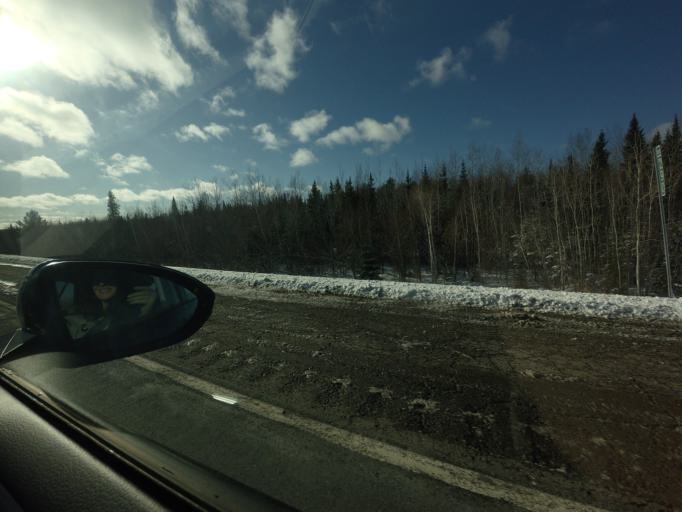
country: CA
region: New Brunswick
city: Fredericton
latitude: 45.8833
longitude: -66.6389
